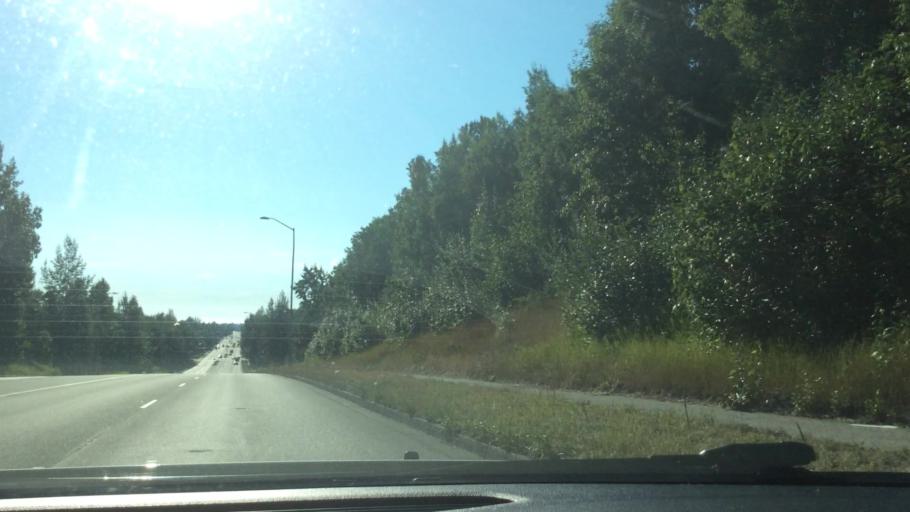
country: US
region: Alaska
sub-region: Anchorage Municipality
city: Anchorage
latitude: 61.2098
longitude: -149.7840
